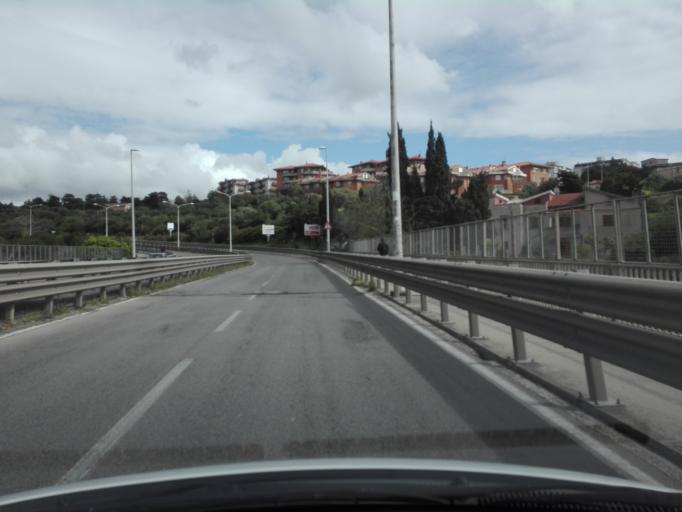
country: IT
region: Sardinia
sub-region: Provincia di Sassari
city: Sassari
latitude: 40.7314
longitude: 8.5718
